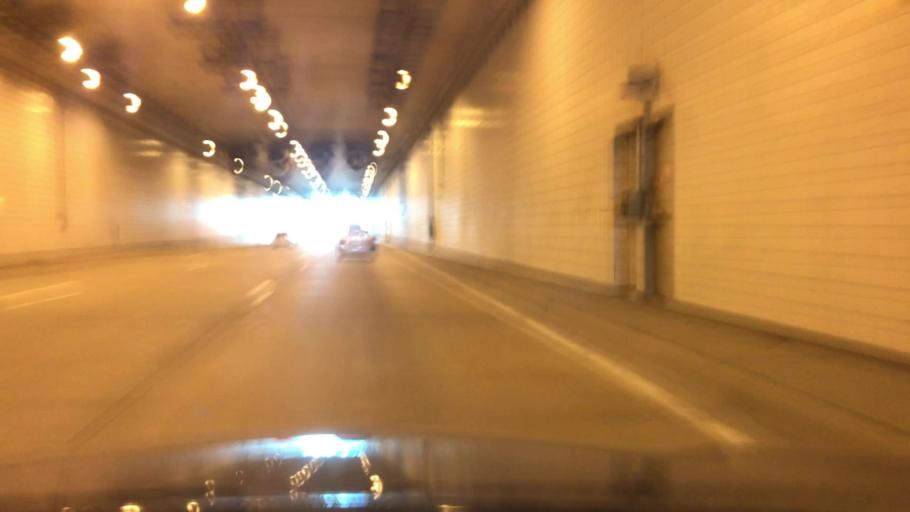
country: US
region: Michigan
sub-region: Wayne County
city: Romulus
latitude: 42.2180
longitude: -83.3467
